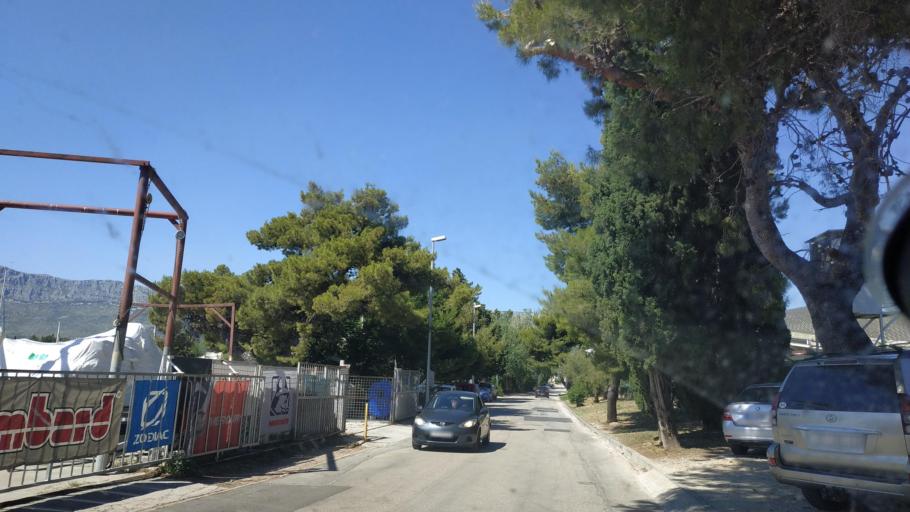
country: HR
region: Splitsko-Dalmatinska
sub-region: Grad Split
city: Split
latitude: 43.5175
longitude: 16.4279
